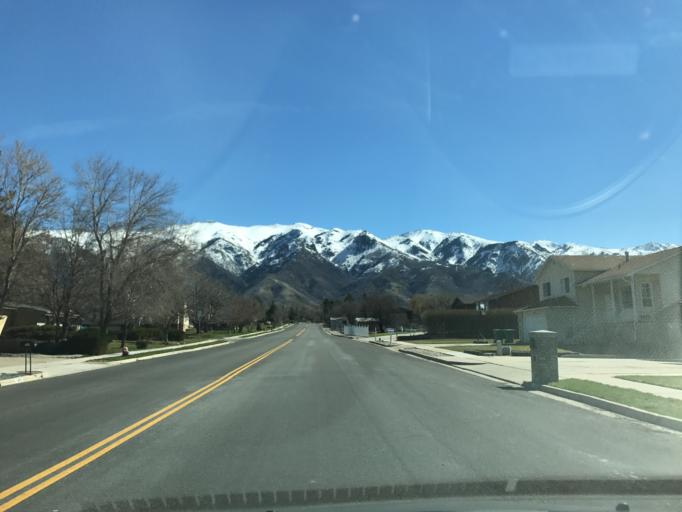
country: US
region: Utah
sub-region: Davis County
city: Layton
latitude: 41.0815
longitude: -111.9389
